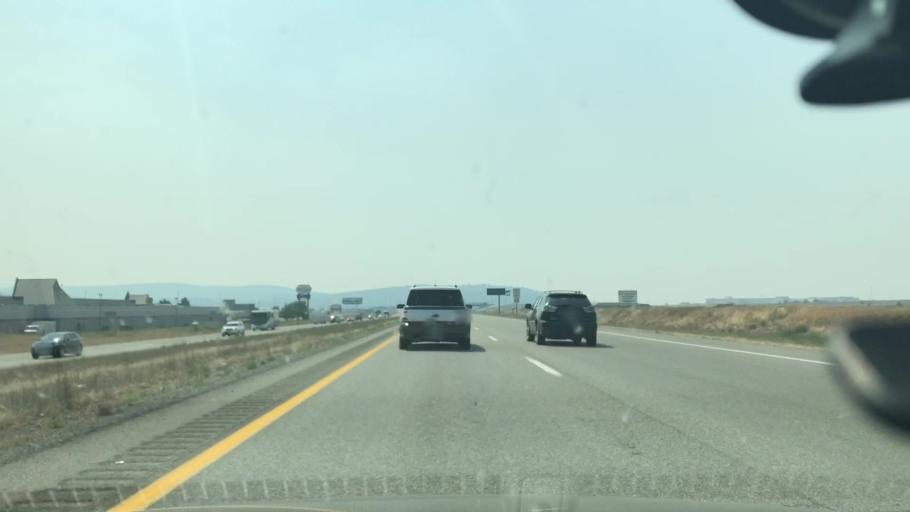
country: US
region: Idaho
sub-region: Kootenai County
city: Post Falls
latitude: 47.7073
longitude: -117.0073
